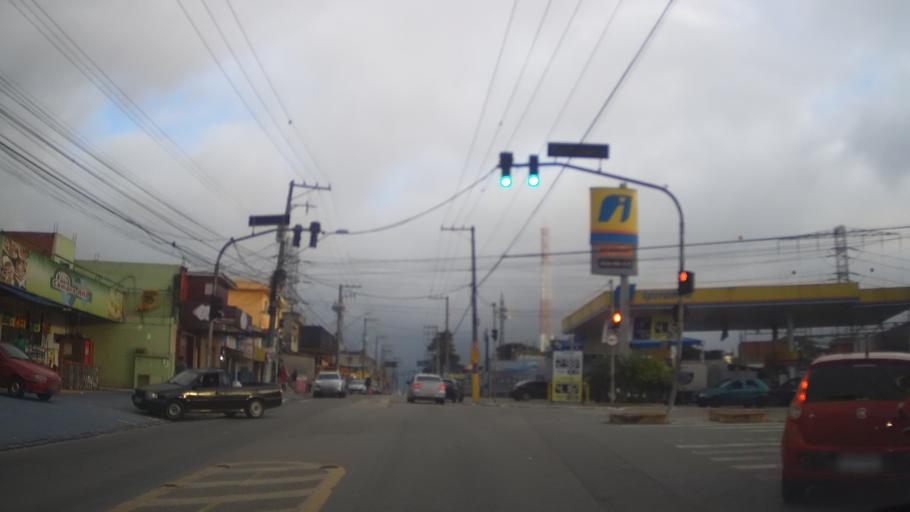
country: BR
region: Sao Paulo
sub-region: Itaquaquecetuba
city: Itaquaquecetuba
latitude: -23.4573
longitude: -46.4230
